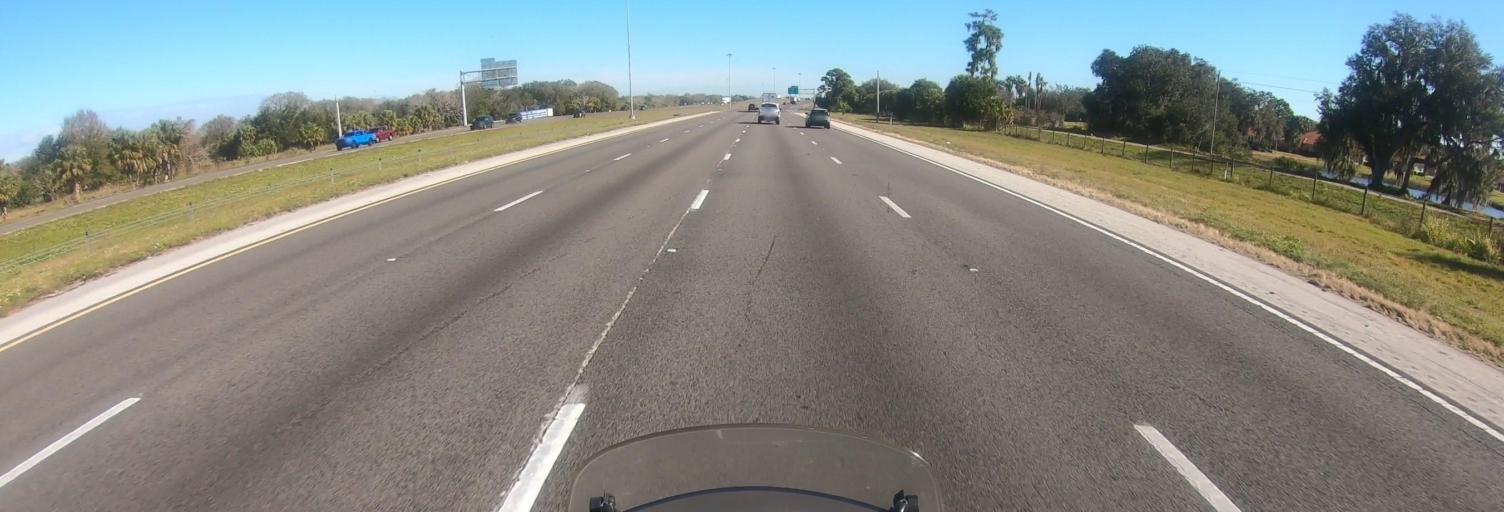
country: US
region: Florida
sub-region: Manatee County
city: Ellenton
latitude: 27.5952
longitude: -82.5088
